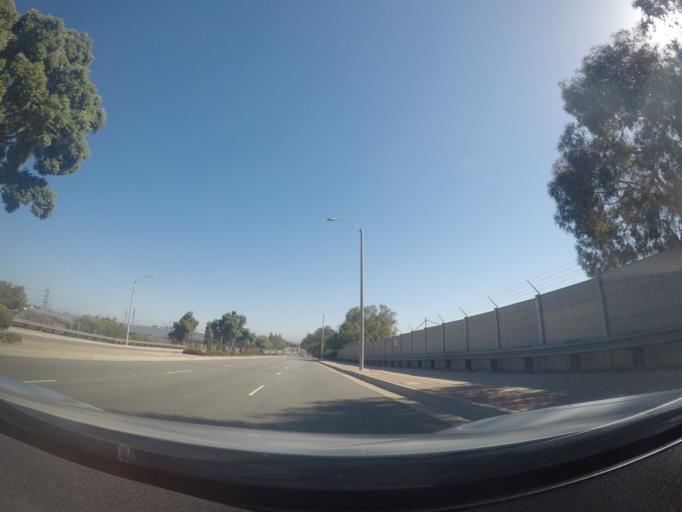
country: US
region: California
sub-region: Los Angeles County
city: Torrance
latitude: 33.8545
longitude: -118.3437
